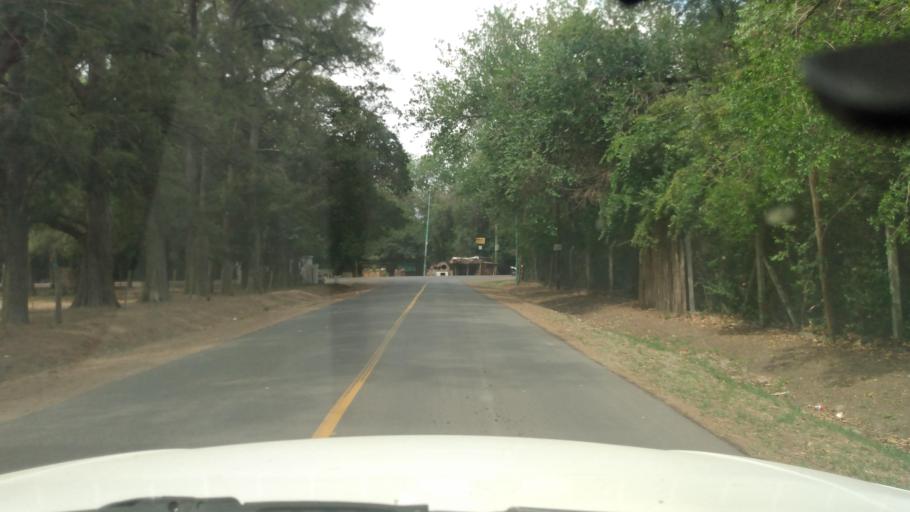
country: AR
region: Buenos Aires
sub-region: Partido de Lujan
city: Lujan
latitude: -34.5532
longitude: -59.1962
